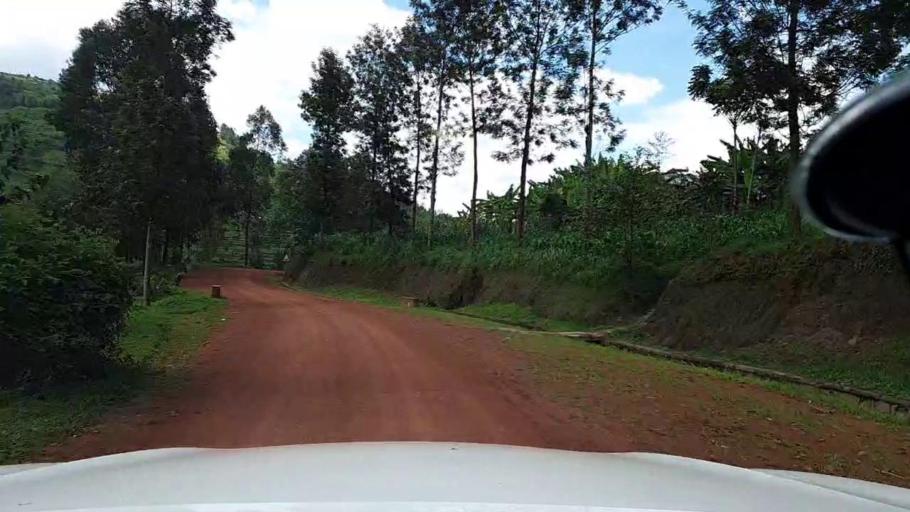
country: RW
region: Northern Province
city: Byumba
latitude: -1.7056
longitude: 29.8415
